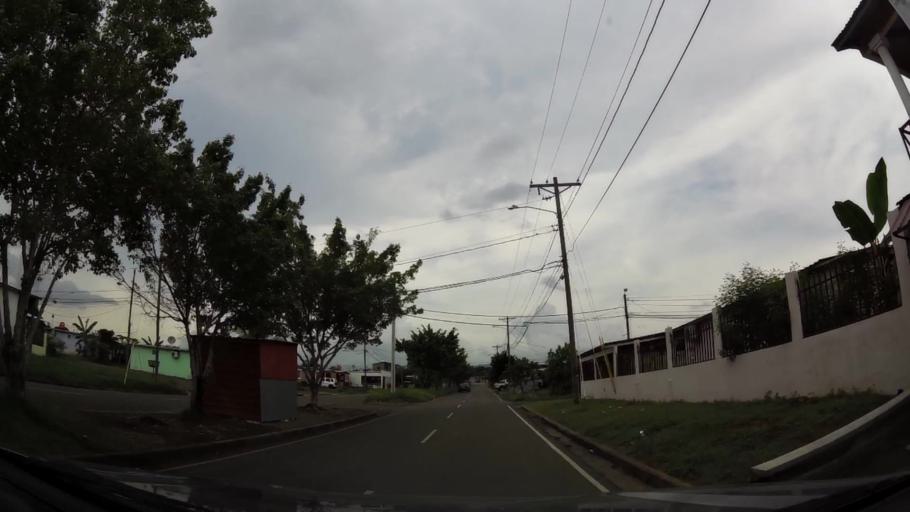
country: PA
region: Panama
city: Cabra Numero Uno
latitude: 9.0898
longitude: -79.3529
